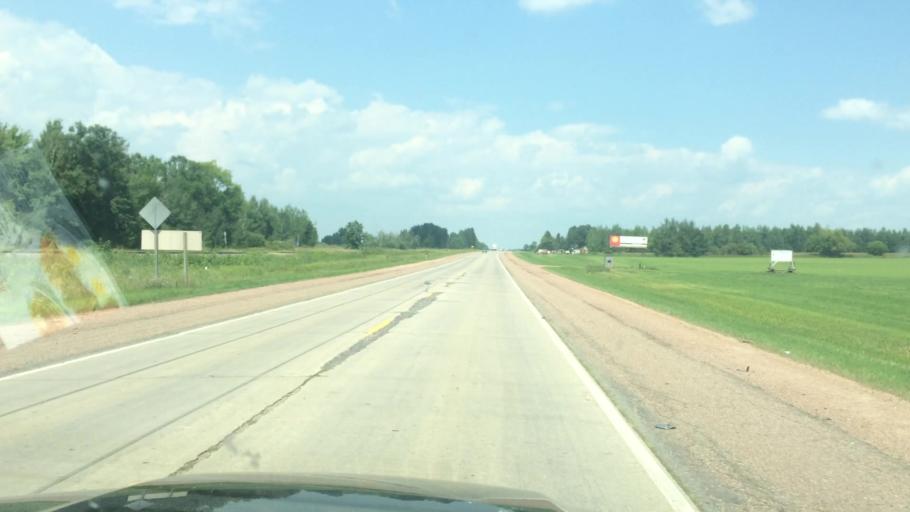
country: US
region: Wisconsin
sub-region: Clark County
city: Colby
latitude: 44.8752
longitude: -90.3157
